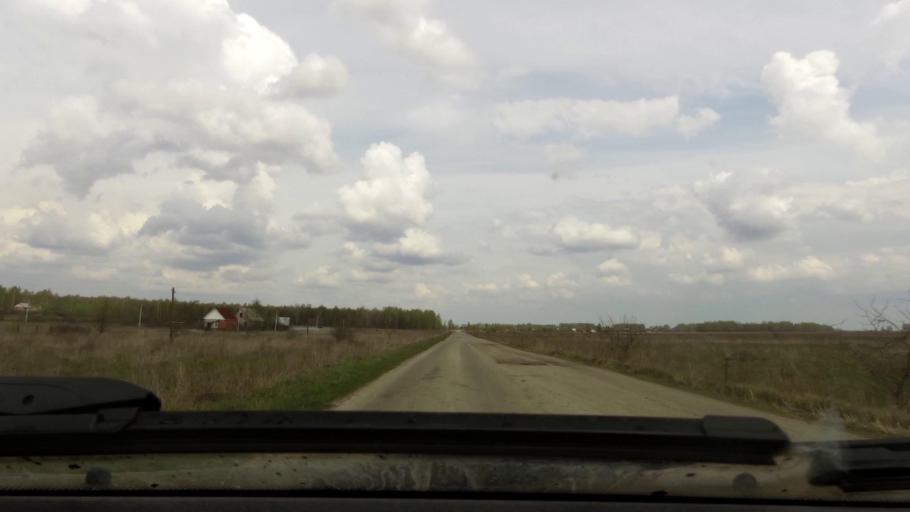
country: RU
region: Rjazan
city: Bagramovo
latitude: 54.7010
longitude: 39.3106
